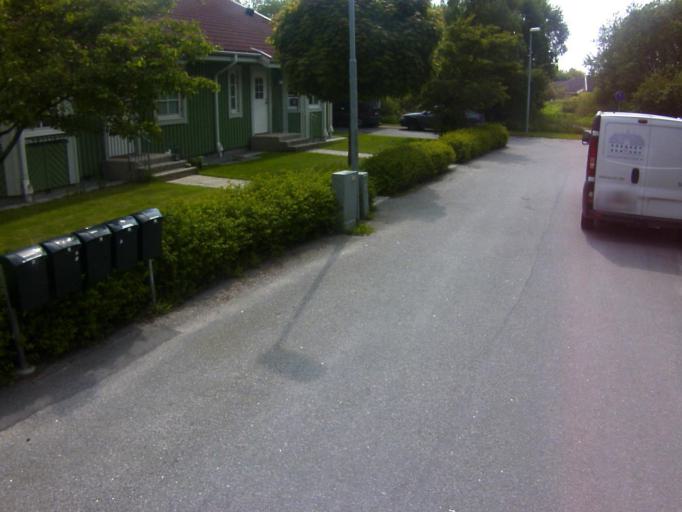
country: SE
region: Blekinge
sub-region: Solvesborgs Kommun
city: Soelvesborg
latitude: 56.0081
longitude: 14.7263
